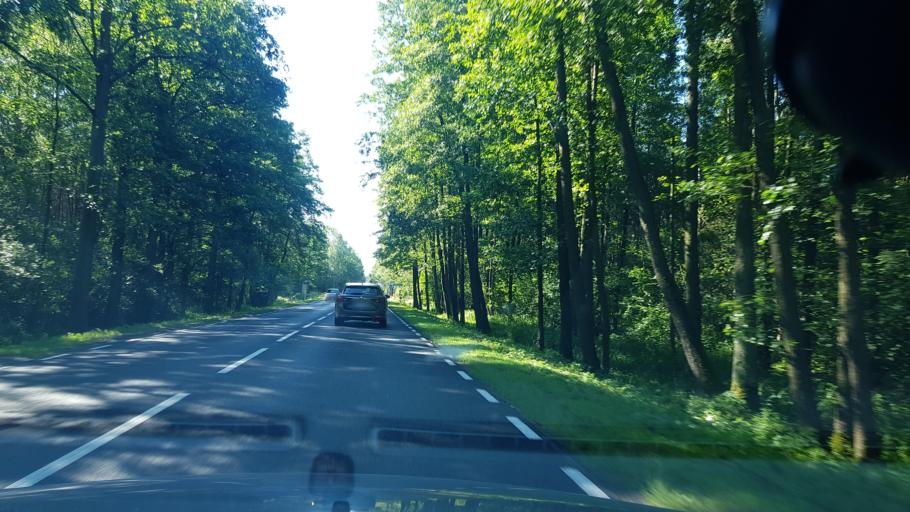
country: PL
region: Masovian Voivodeship
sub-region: Powiat wyszkowski
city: Branszczyk
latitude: 52.5780
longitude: 21.5357
